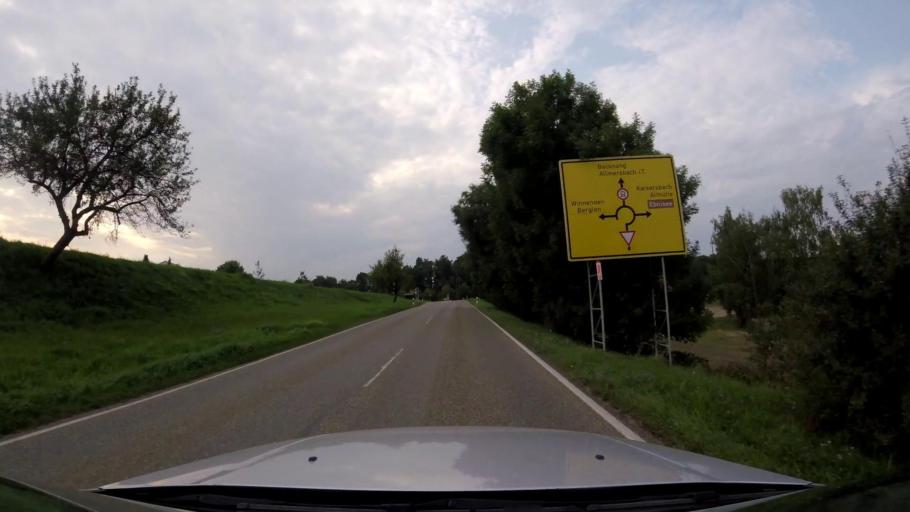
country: DE
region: Baden-Wuerttemberg
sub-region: Regierungsbezirk Stuttgart
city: Rudersberg
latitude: 48.8958
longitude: 9.4995
